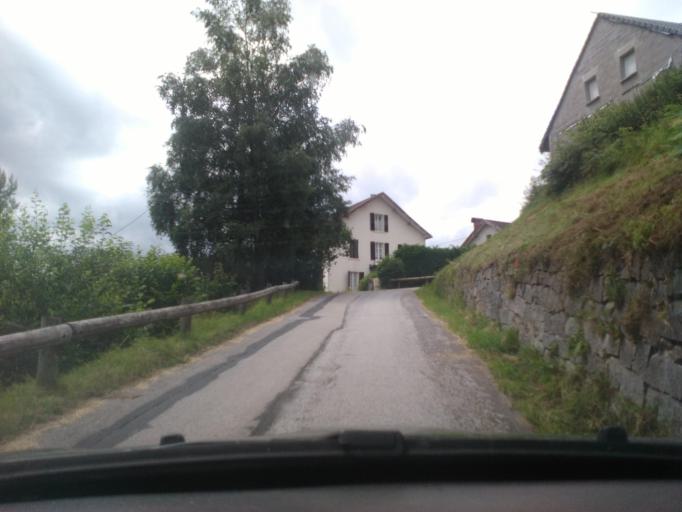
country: FR
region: Lorraine
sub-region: Departement des Vosges
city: Gerardmer
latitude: 48.0826
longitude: 6.8899
